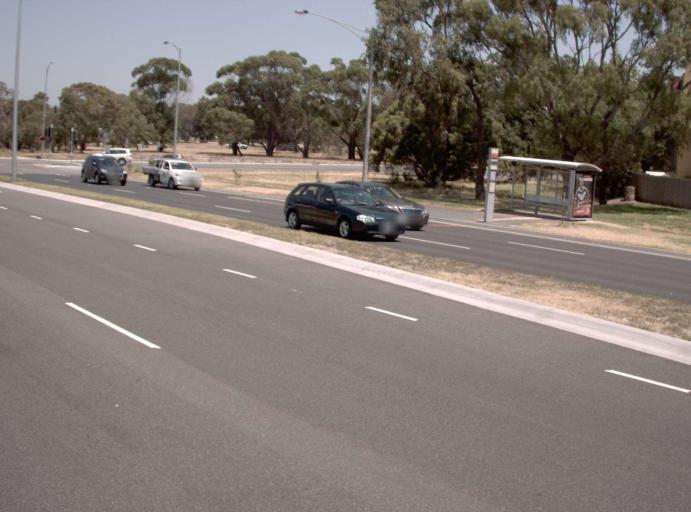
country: AU
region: Victoria
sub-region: Kingston
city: Dingley Village
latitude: -37.9816
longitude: 145.1465
